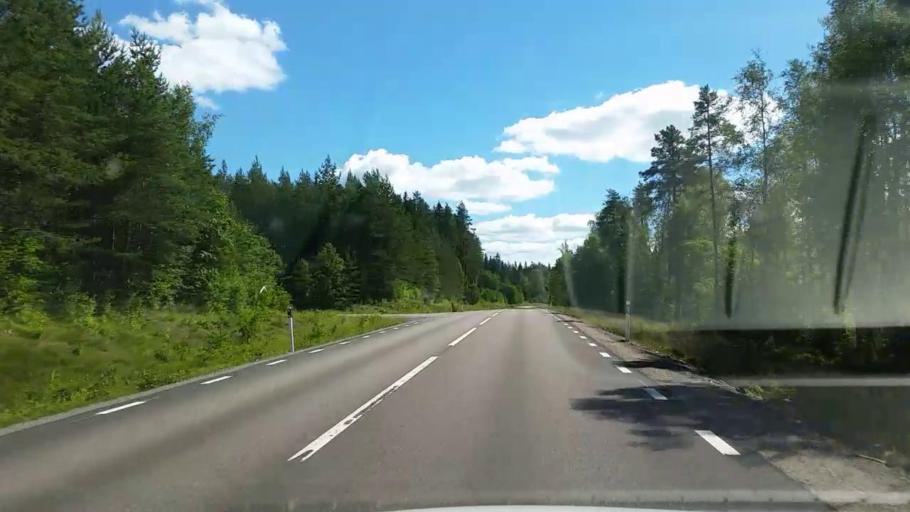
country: SE
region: Dalarna
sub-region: Faluns Kommun
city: Svardsjo
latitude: 60.7697
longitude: 15.7554
